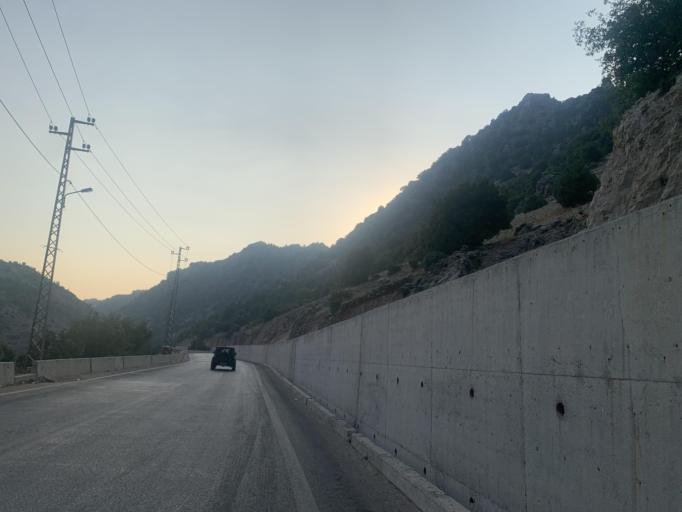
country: LB
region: Liban-Nord
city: Amioun
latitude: 34.1360
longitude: 35.8315
